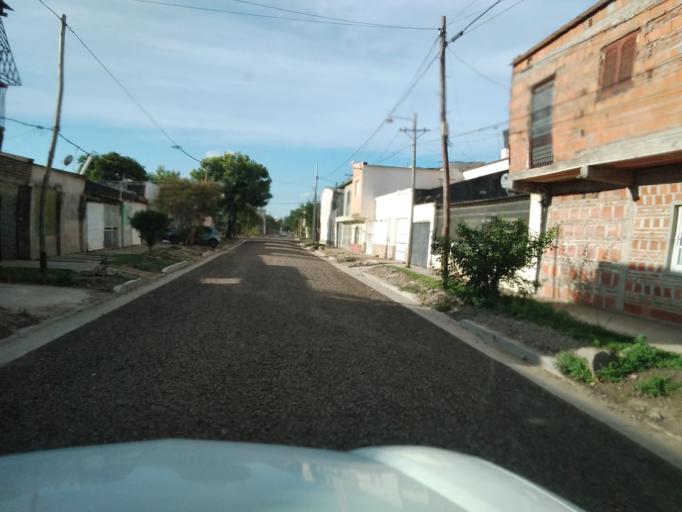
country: AR
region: Corrientes
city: Corrientes
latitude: -27.4911
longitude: -58.8467
